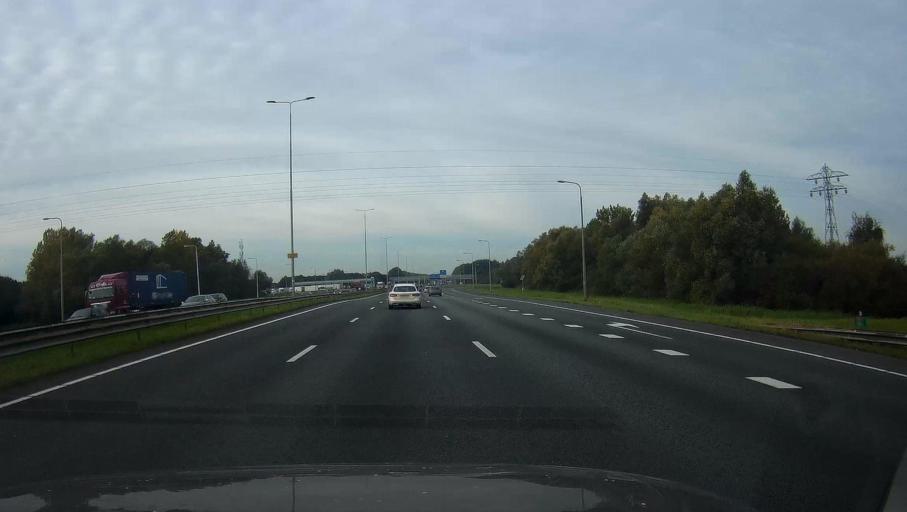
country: NL
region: South Holland
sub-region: Gemeente Hendrik-Ido-Ambacht
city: Hendrik-Ido-Ambacht
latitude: 51.8560
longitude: 4.6316
